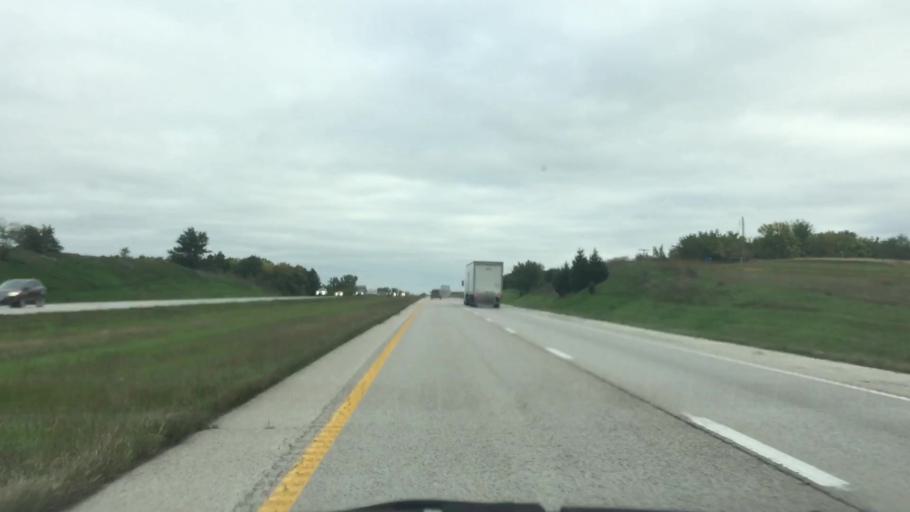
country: US
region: Missouri
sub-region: Clinton County
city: Cameron
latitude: 39.7080
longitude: -94.2255
